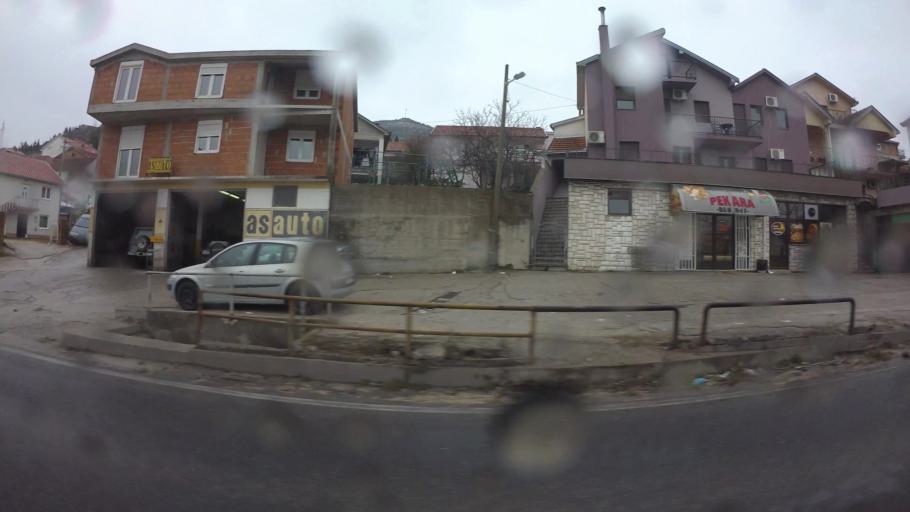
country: BA
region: Federation of Bosnia and Herzegovina
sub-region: Hercegovacko-Bosanski Kanton
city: Mostar
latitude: 43.3475
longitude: 17.8168
